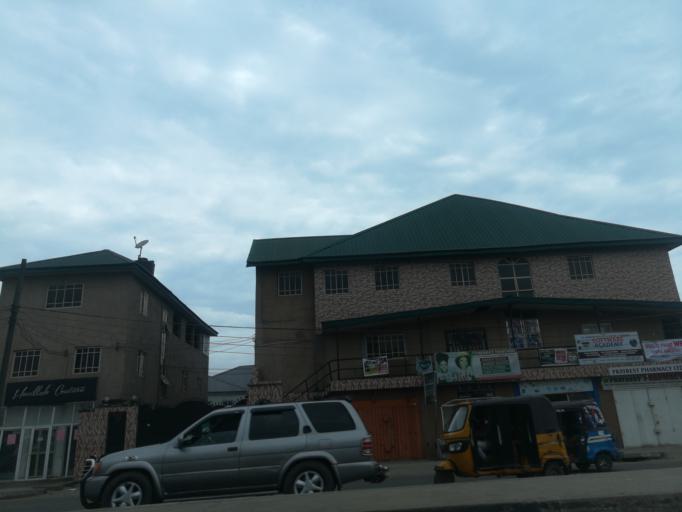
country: NG
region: Rivers
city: Port Harcourt
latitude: 4.8299
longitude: 6.9764
